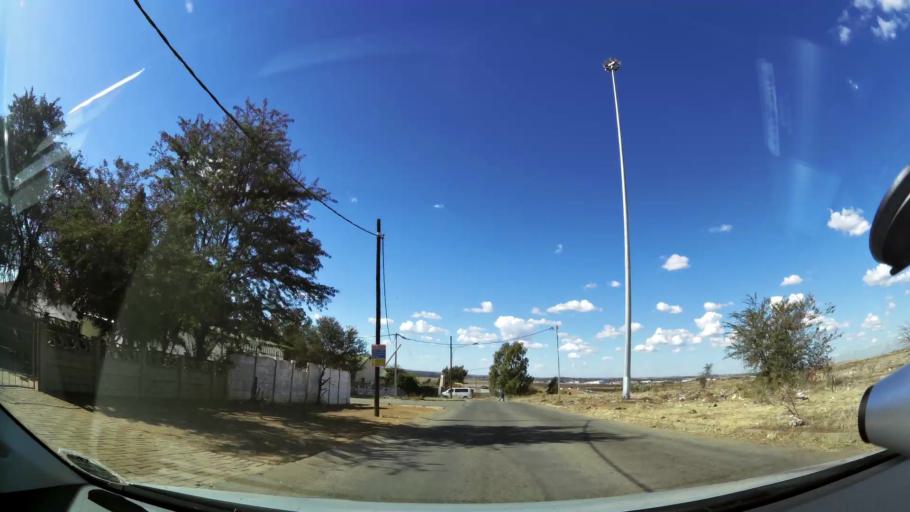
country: ZA
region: North-West
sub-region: Dr Kenneth Kaunda District Municipality
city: Klerksdorp
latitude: -26.8743
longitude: 26.5950
